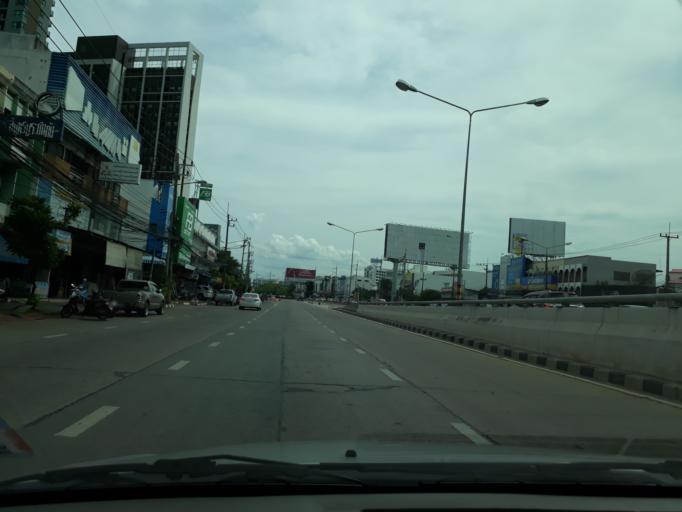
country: TH
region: Khon Kaen
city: Khon Kaen
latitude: 16.4368
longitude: 102.8266
